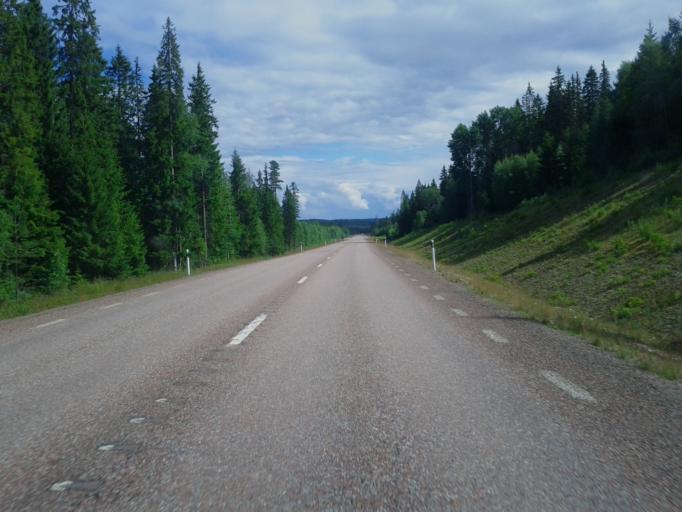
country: SE
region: Dalarna
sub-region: Rattviks Kommun
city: Raettvik
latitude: 60.8318
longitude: 15.2380
